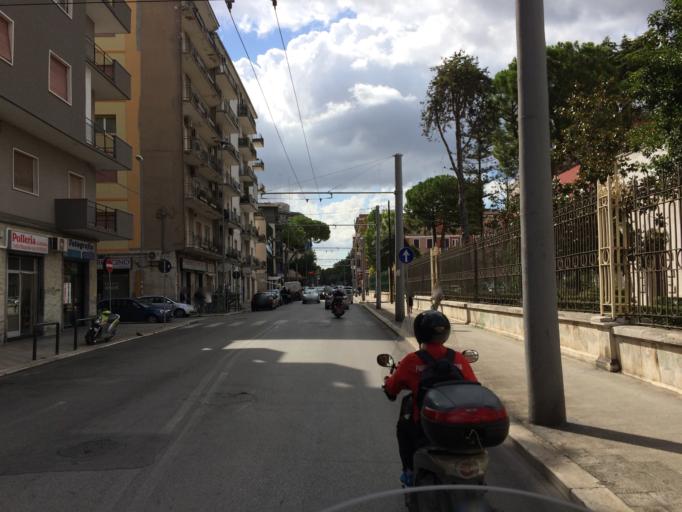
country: IT
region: Apulia
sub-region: Provincia di Bari
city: Bari
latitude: 41.1068
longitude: 16.8718
